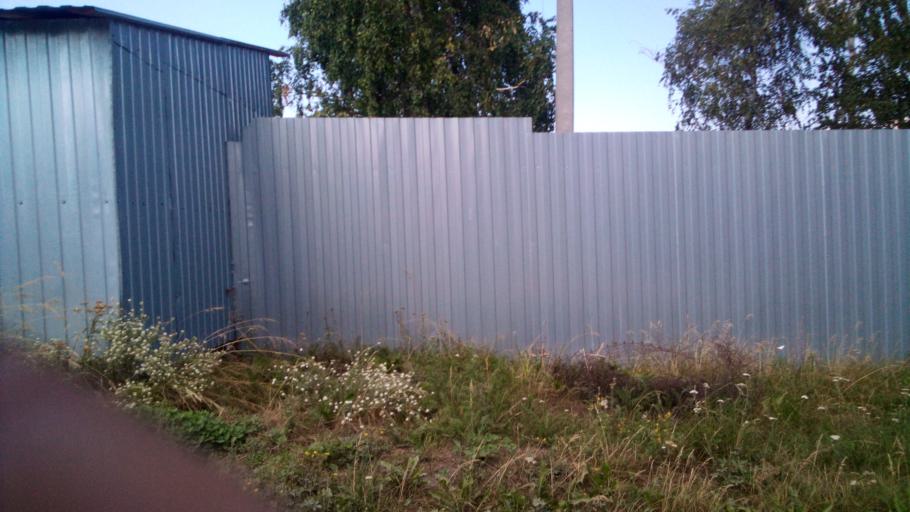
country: RU
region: Chelyabinsk
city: Ozersk
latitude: 55.7880
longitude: 60.7487
